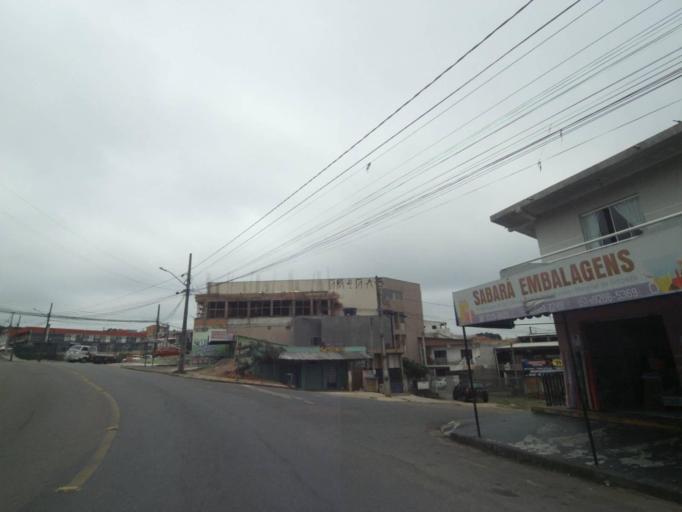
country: BR
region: Parana
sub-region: Curitiba
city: Curitiba
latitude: -25.4997
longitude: -49.3476
